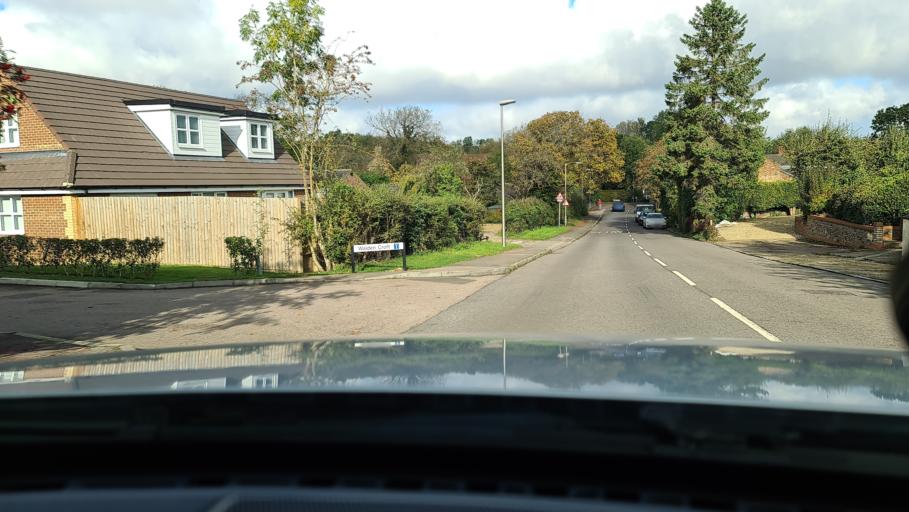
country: GB
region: England
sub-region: Milton Keynes
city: Simpson
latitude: 52.0148
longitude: -0.7168
